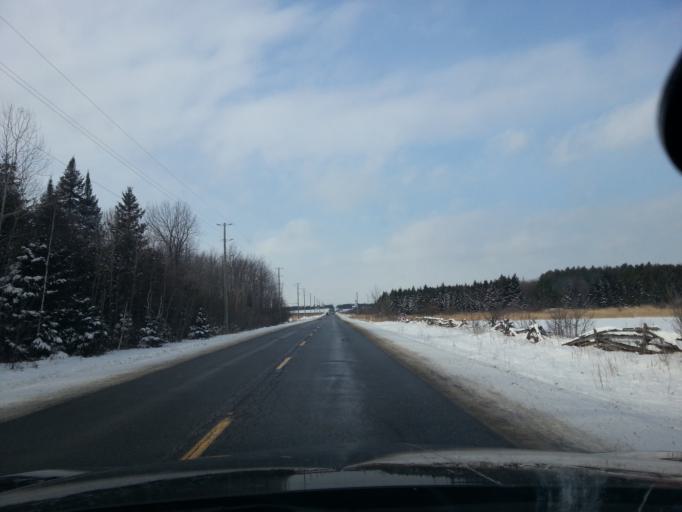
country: CA
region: Ontario
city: Carleton Place
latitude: 45.1627
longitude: -76.0398
